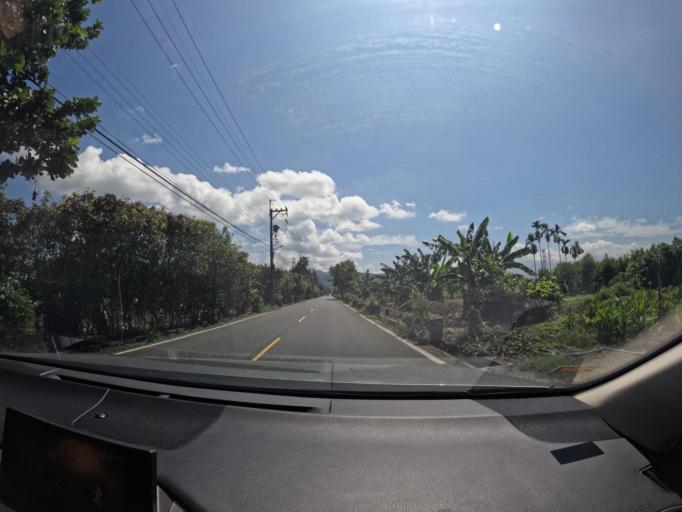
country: TW
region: Taiwan
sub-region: Hualien
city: Hualian
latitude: 23.5806
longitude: 121.3700
